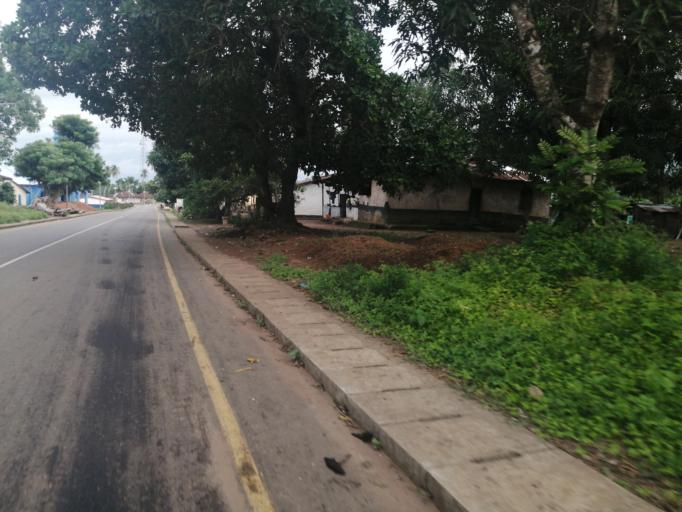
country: SL
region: Northern Province
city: Port Loko
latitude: 8.7713
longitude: -12.7914
